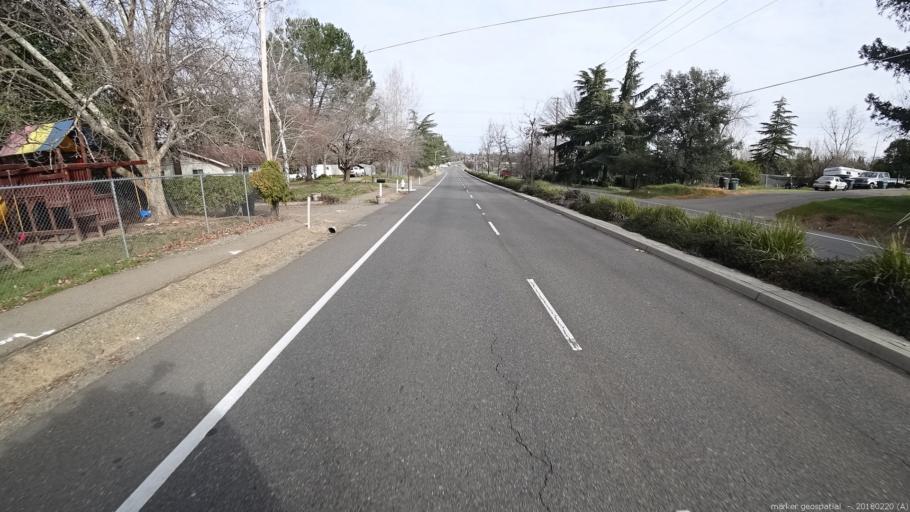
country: US
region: California
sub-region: Sacramento County
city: Orangevale
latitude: 38.7139
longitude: -121.2258
